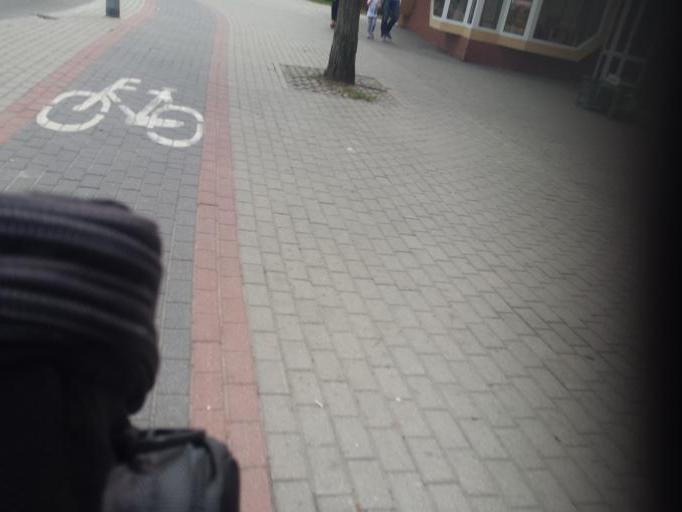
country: PL
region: Warmian-Masurian Voivodeship
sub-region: Powiat ilawski
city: Ilawa
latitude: 53.5949
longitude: 19.5655
